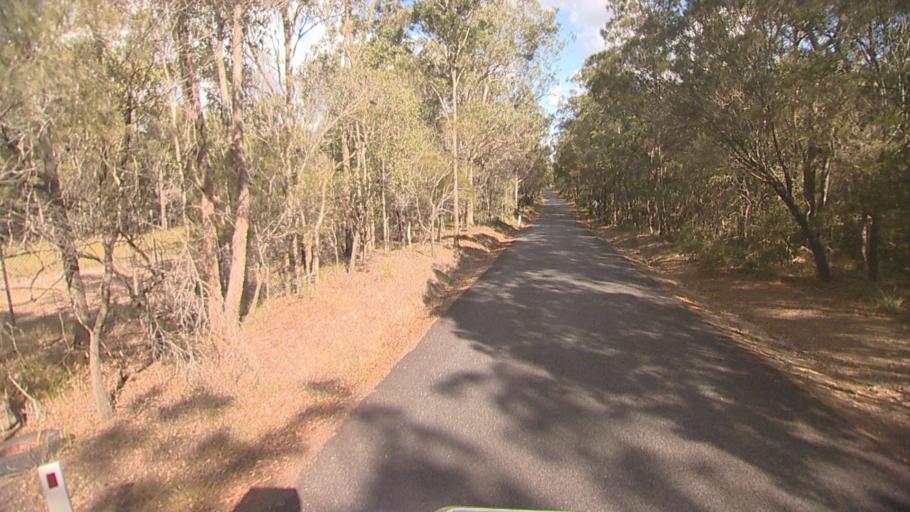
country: AU
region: Queensland
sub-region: Logan
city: Beenleigh
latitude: -27.6523
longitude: 153.2302
